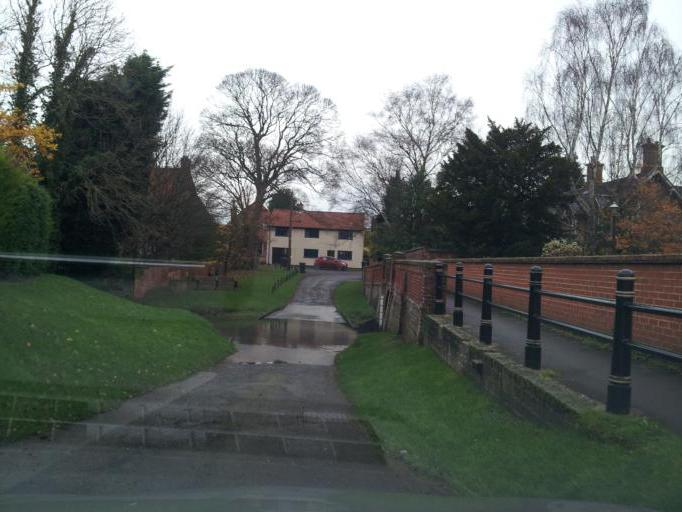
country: GB
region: England
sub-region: Lincolnshire
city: Long Bennington
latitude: 52.9433
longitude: -0.8032
